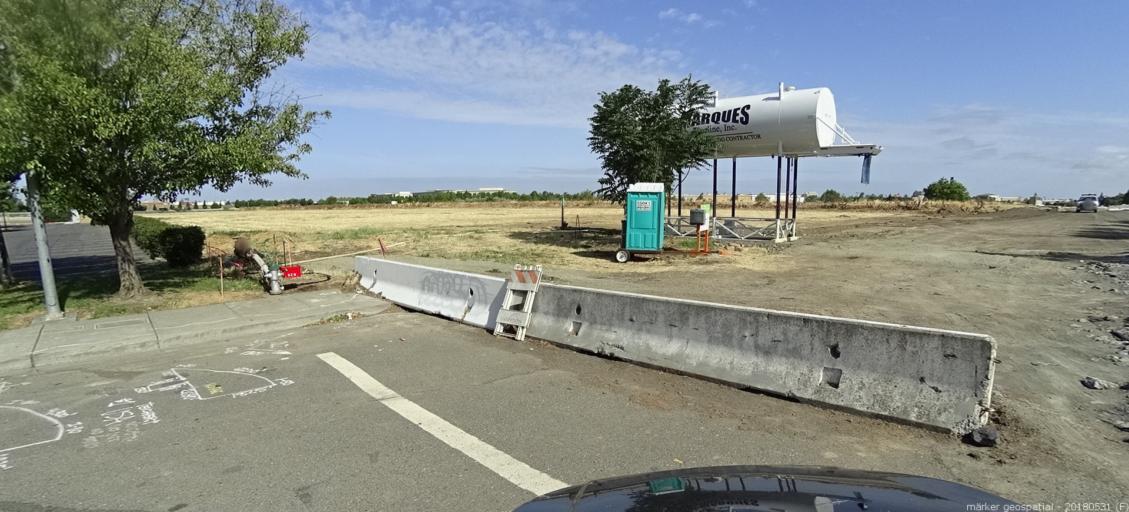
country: US
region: California
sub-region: Sacramento County
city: Sacramento
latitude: 38.6339
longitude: -121.4935
